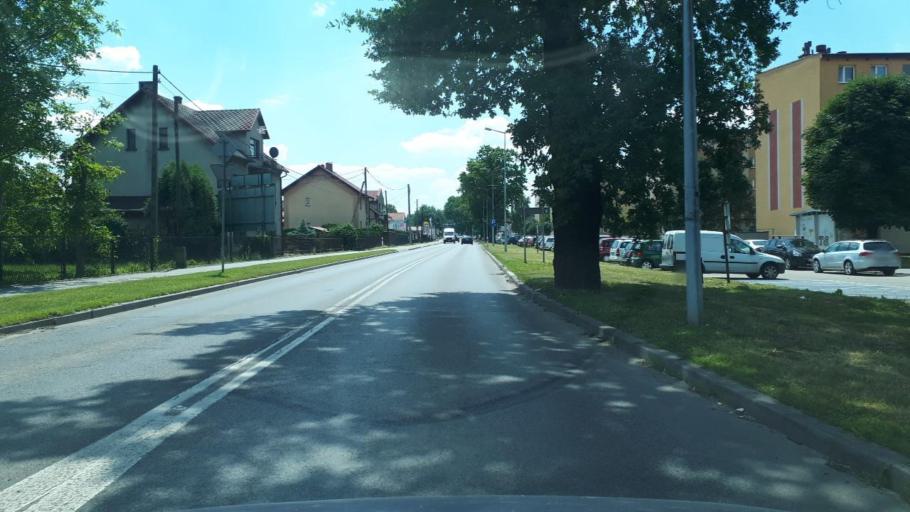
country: PL
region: Lesser Poland Voivodeship
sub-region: Powiat oswiecimski
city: Brzeszcze
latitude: 49.9718
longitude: 19.1387
